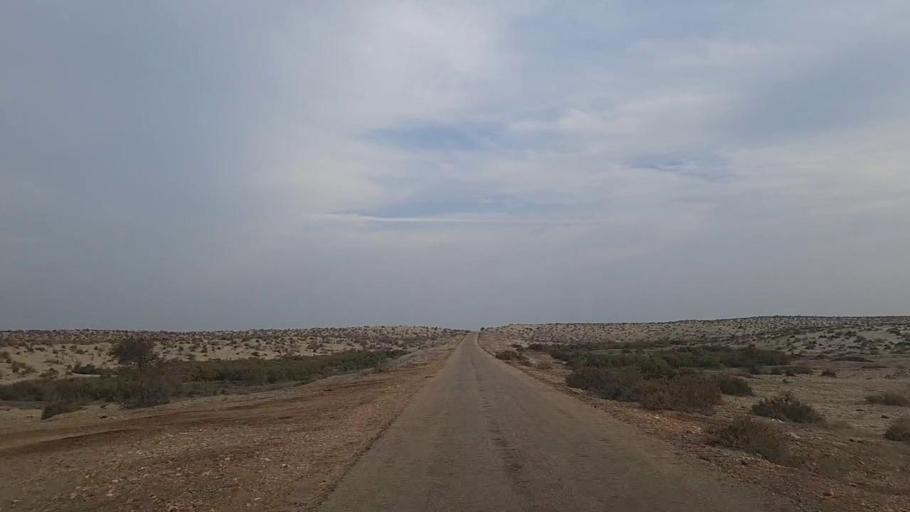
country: PK
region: Sindh
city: Daur
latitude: 26.5107
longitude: 68.5076
